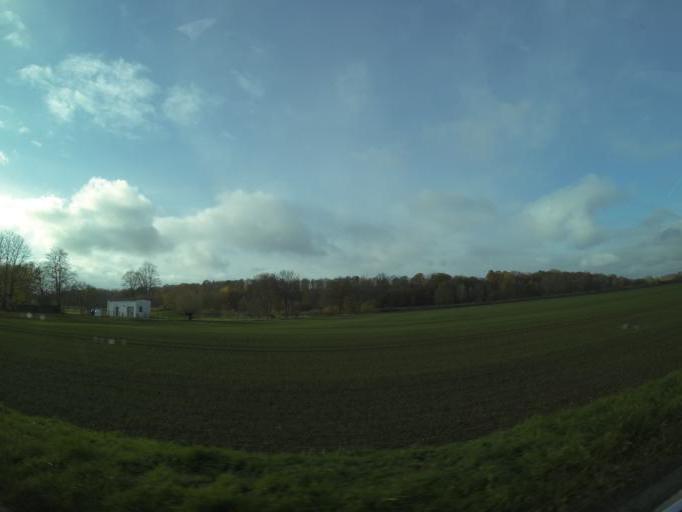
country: DE
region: Thuringia
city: Gossnitz
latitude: 50.9129
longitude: 12.4429
